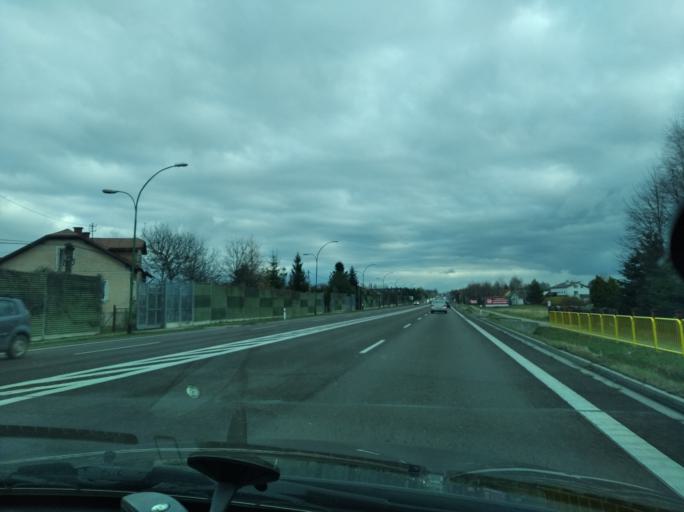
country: PL
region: Subcarpathian Voivodeship
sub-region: Powiat lancucki
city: Kraczkowa
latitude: 50.0453
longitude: 22.1427
